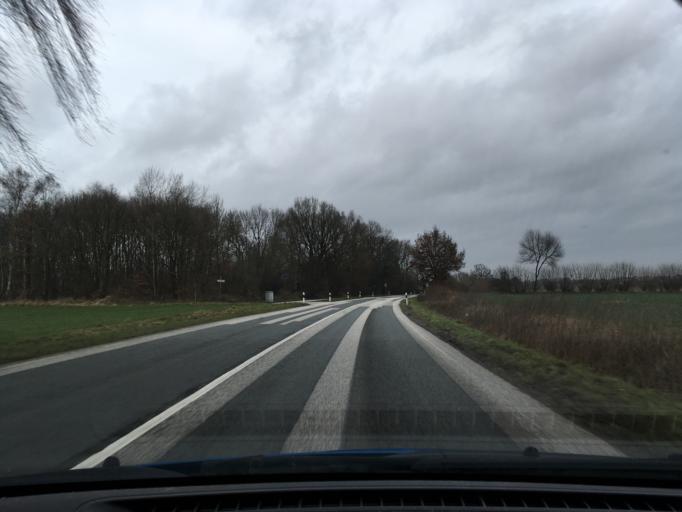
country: DE
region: Schleswig-Holstein
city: Kruzen
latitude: 53.4140
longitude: 10.5361
